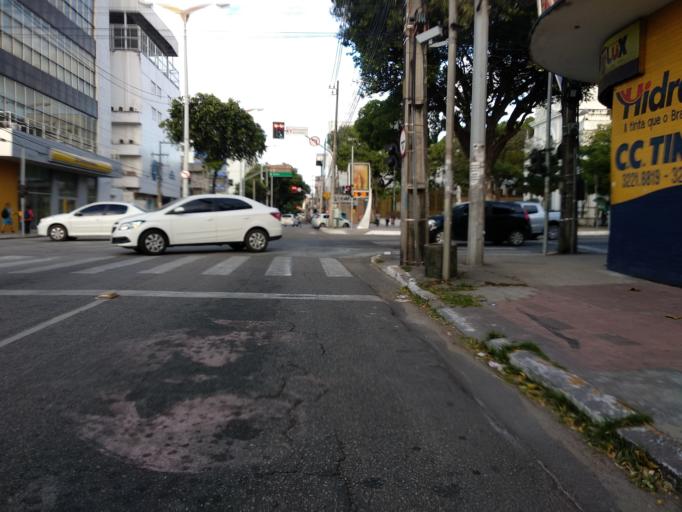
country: BR
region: Ceara
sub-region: Fortaleza
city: Fortaleza
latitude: -3.7316
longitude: -38.5307
